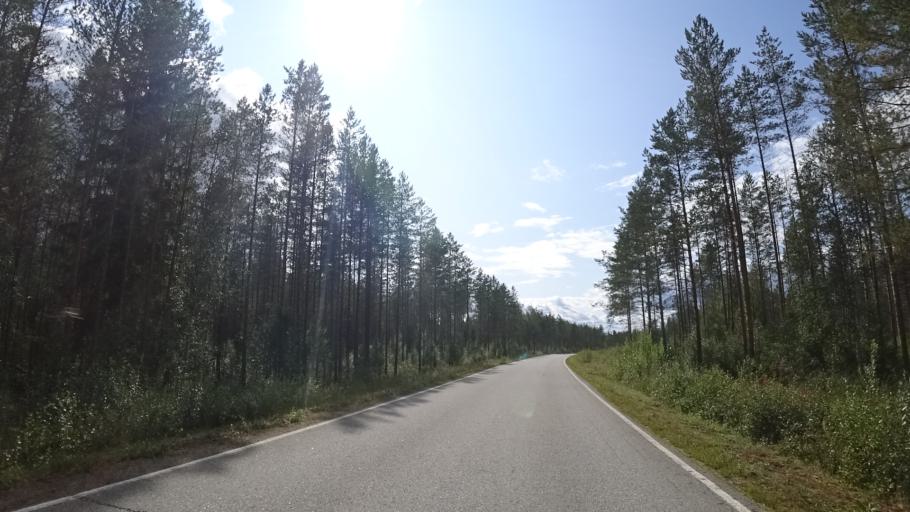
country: FI
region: North Karelia
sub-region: Joensuu
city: Ilomantsi
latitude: 62.4138
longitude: 31.0038
